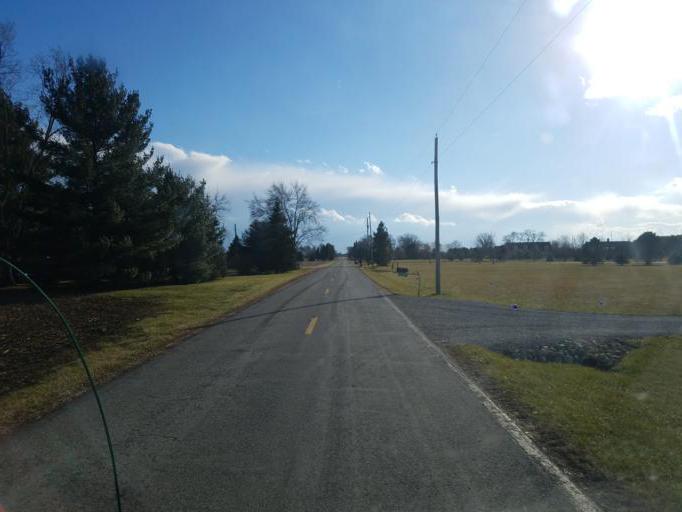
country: US
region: Ohio
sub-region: Marion County
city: Prospect
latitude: 40.4095
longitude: -83.1437
